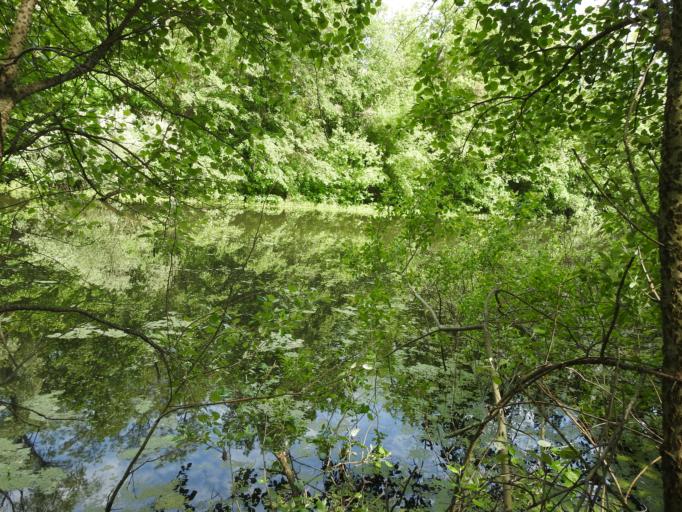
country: RU
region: Saratov
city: Engel's
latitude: 51.4694
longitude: 46.0736
